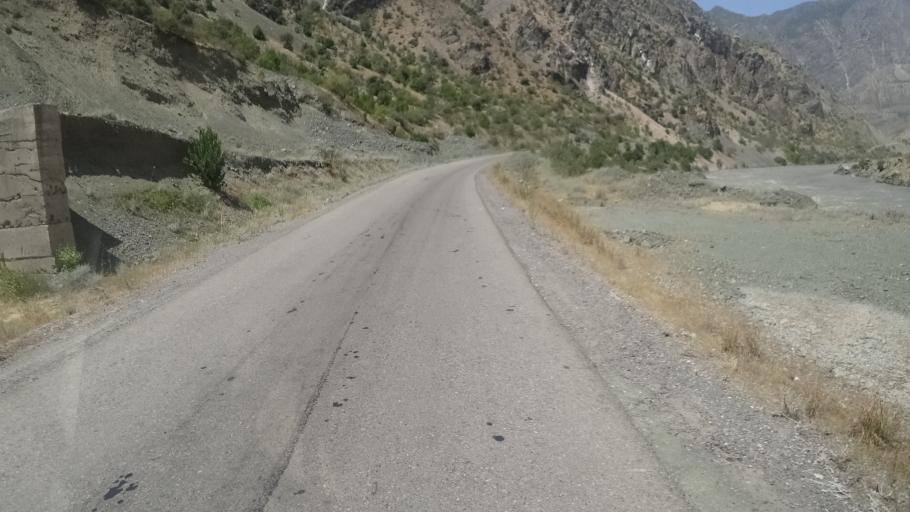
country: AF
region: Badakhshan
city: Deh Khwahan
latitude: 37.9489
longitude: 70.2687
